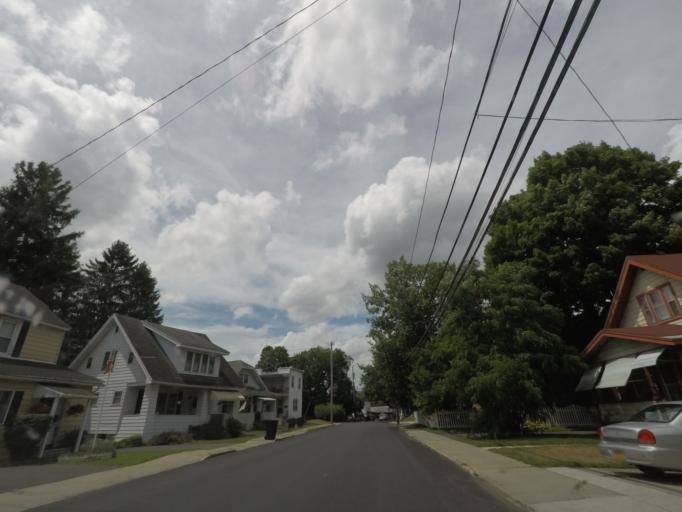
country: US
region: New York
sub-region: Rensselaer County
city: Wynantskill
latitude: 42.7075
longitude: -73.6585
